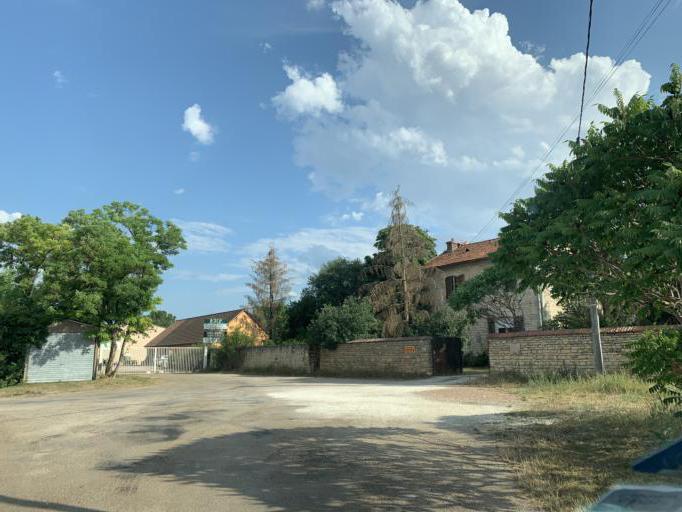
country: FR
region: Bourgogne
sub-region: Departement de l'Yonne
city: Fontenailles
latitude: 47.5432
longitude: 3.4211
